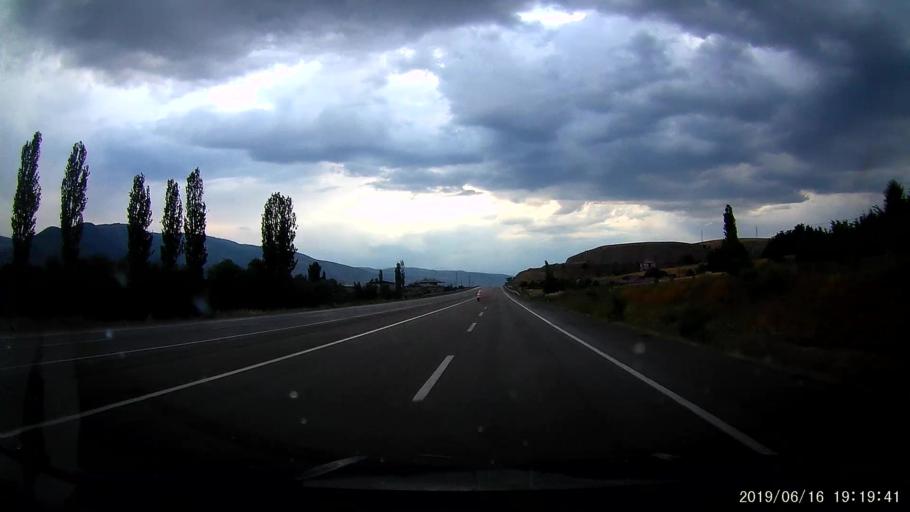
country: TR
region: Sivas
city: Akincilar
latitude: 40.0948
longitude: 38.4218
